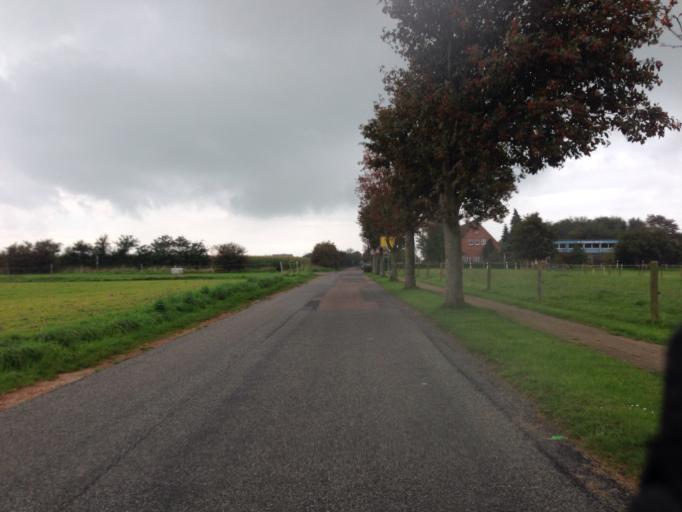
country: DE
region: Schleswig-Holstein
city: Midlum
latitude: 54.7117
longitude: 8.5238
